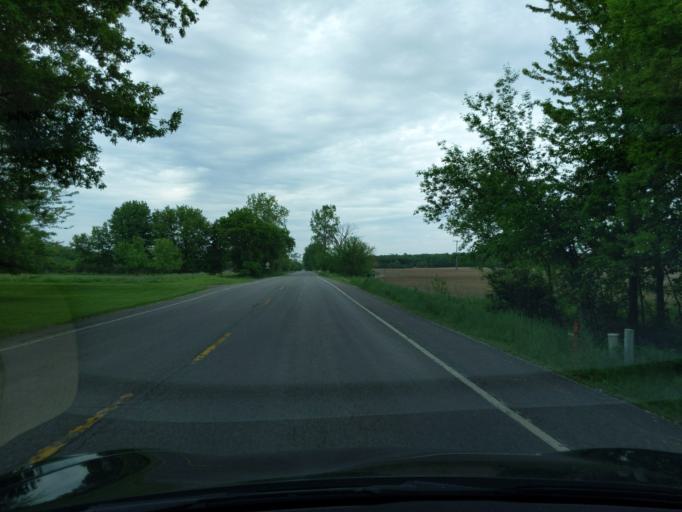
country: US
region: Michigan
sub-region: Ingham County
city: Mason
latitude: 42.6013
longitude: -84.3577
